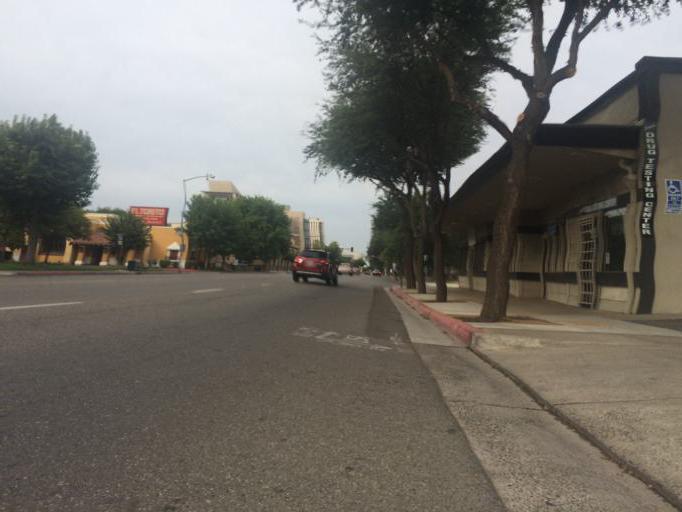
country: US
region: California
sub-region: Fresno County
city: Fresno
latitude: 36.7408
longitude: -119.7805
